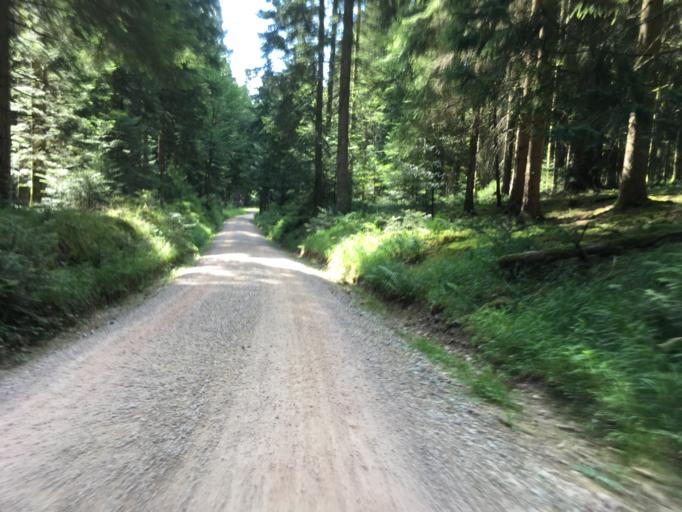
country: DE
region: Baden-Wuerttemberg
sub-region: Karlsruhe Region
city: Lossburg
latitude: 48.4319
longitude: 8.4297
